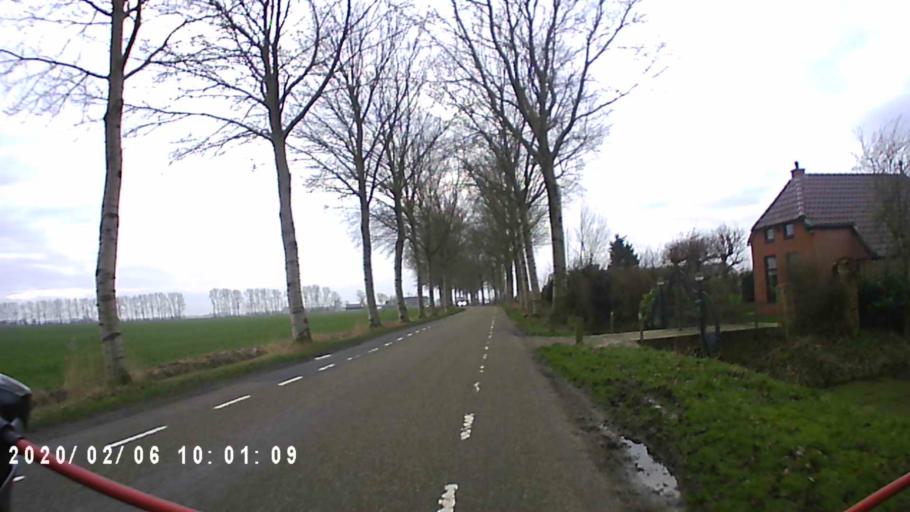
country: NL
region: Groningen
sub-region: Gemeente Zuidhorn
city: Aduard
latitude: 53.2639
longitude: 6.4898
